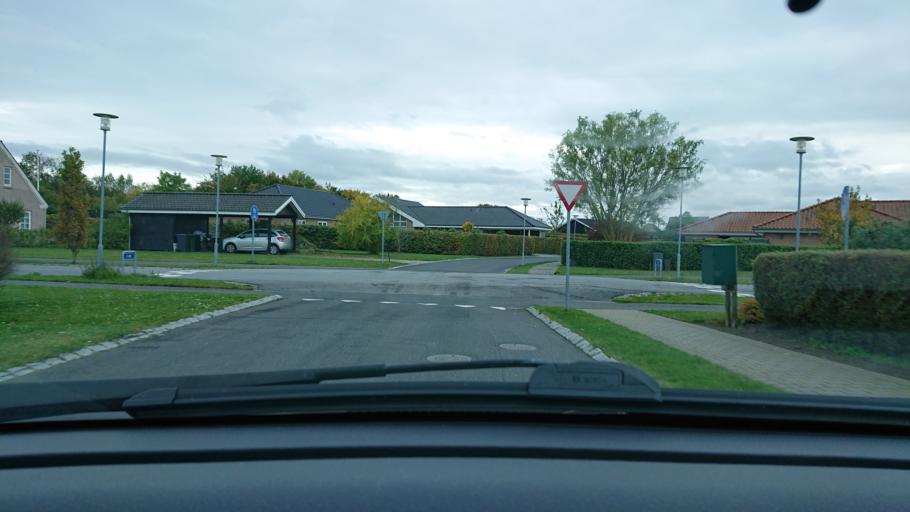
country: DK
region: South Denmark
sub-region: Nyborg Kommune
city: Nyborg
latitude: 55.3074
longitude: 10.7576
